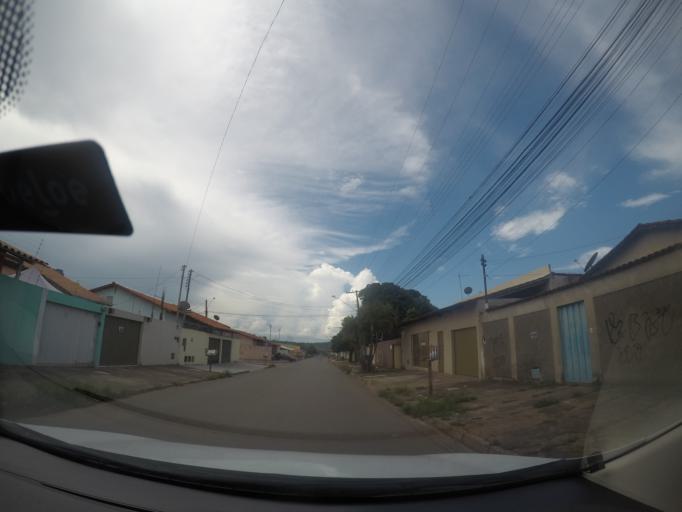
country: BR
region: Goias
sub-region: Goiania
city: Goiania
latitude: -16.7018
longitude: -49.3568
